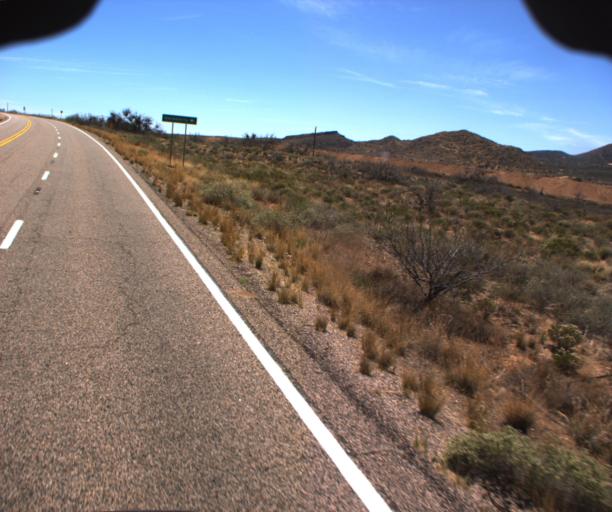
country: US
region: Arizona
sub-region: Mohave County
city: New Kingman-Butler
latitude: 35.3763
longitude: -113.7248
